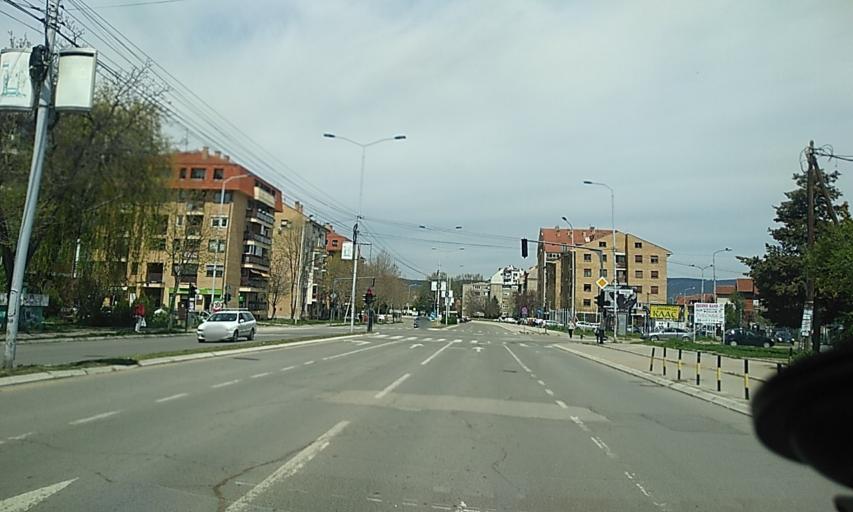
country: RS
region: Central Serbia
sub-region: Nisavski Okrug
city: Nis
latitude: 43.3131
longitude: 21.9277
